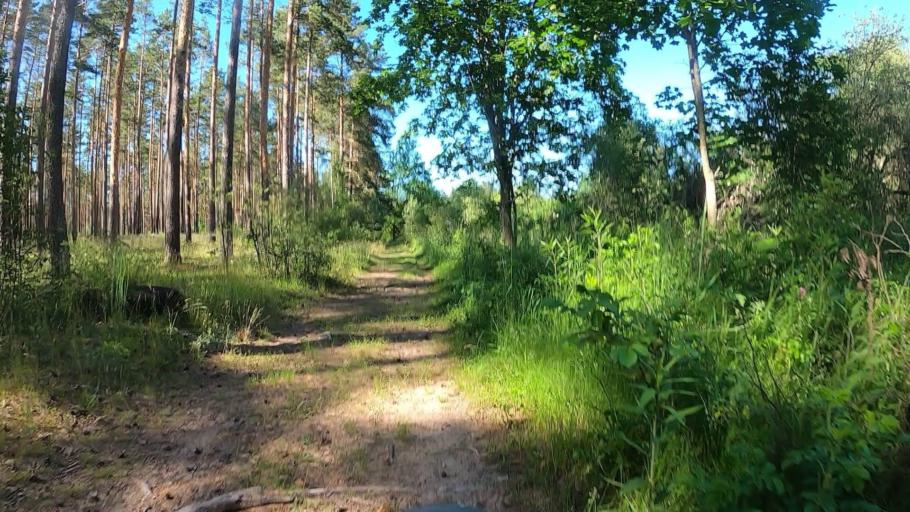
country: LV
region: Riga
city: Bergi
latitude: 57.0233
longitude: 24.2482
